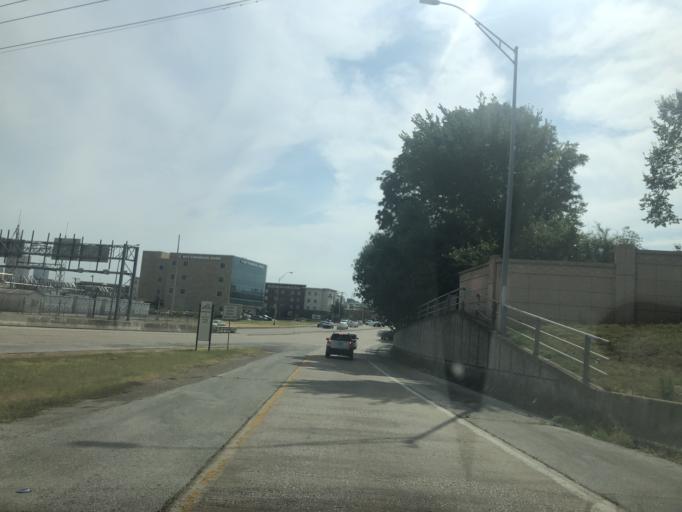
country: US
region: Texas
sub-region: Tarrant County
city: Fort Worth
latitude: 32.7338
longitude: -97.3546
